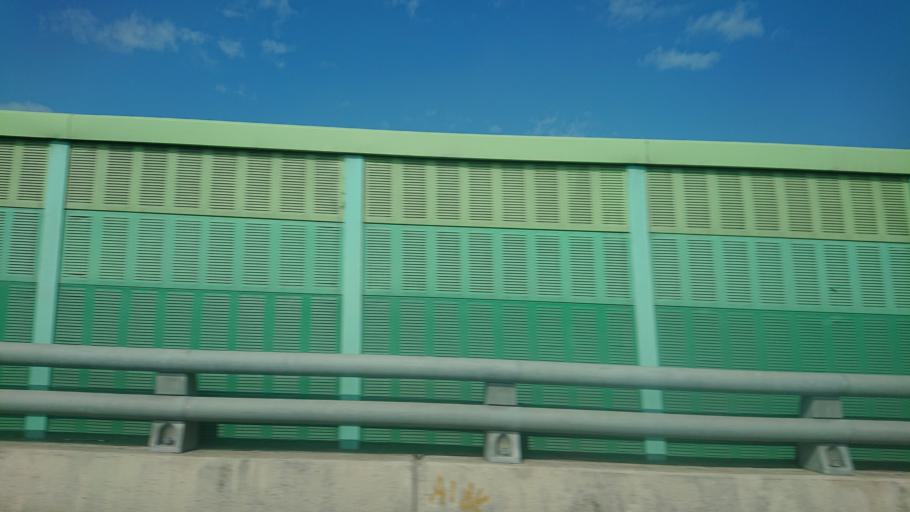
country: TW
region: Taiwan
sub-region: Changhua
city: Chang-hua
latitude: 24.0420
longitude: 120.4050
